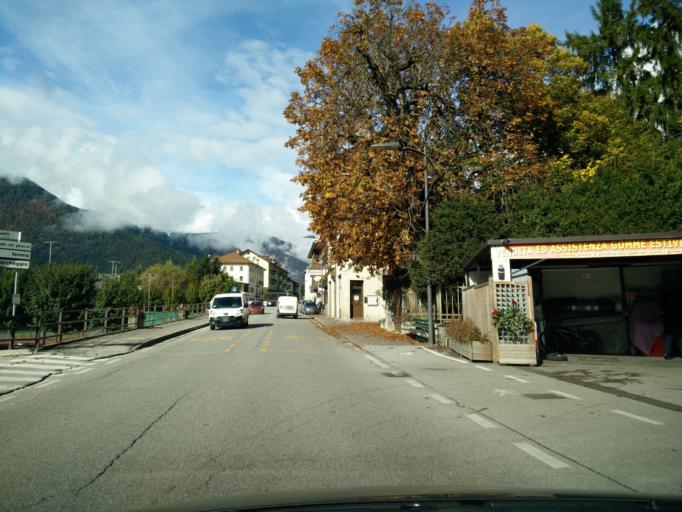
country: IT
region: Veneto
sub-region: Provincia di Belluno
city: Auronzo
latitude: 46.5489
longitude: 12.4488
